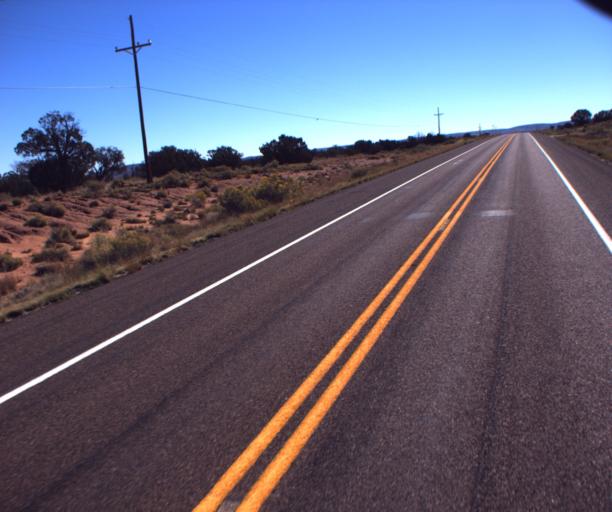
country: US
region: Arizona
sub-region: Apache County
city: Saint Johns
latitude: 34.6408
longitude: -109.6932
